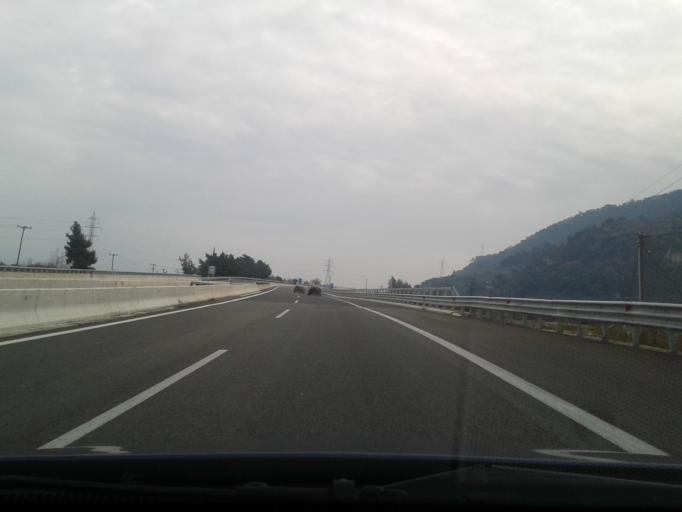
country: GR
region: West Greece
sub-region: Nomos Achaias
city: Temeni
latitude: 38.1841
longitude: 22.1908
